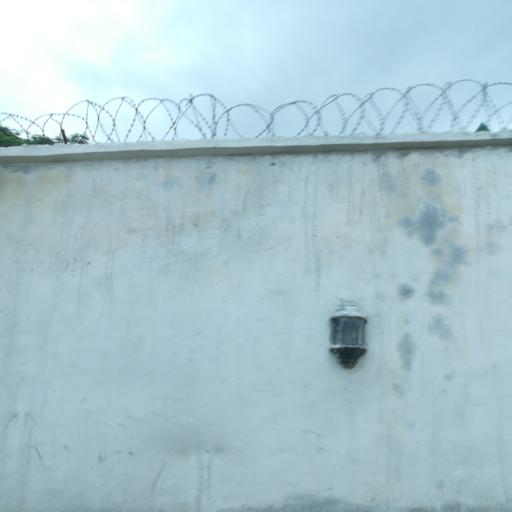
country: NG
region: Rivers
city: Port Harcourt
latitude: 4.8112
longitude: 7.0615
